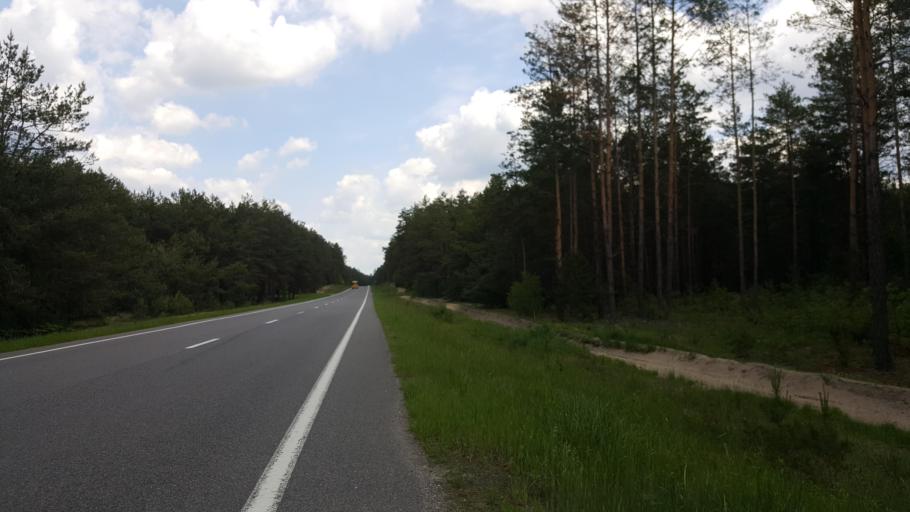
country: BY
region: Brest
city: Zhabinka
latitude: 52.4298
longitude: 24.1252
